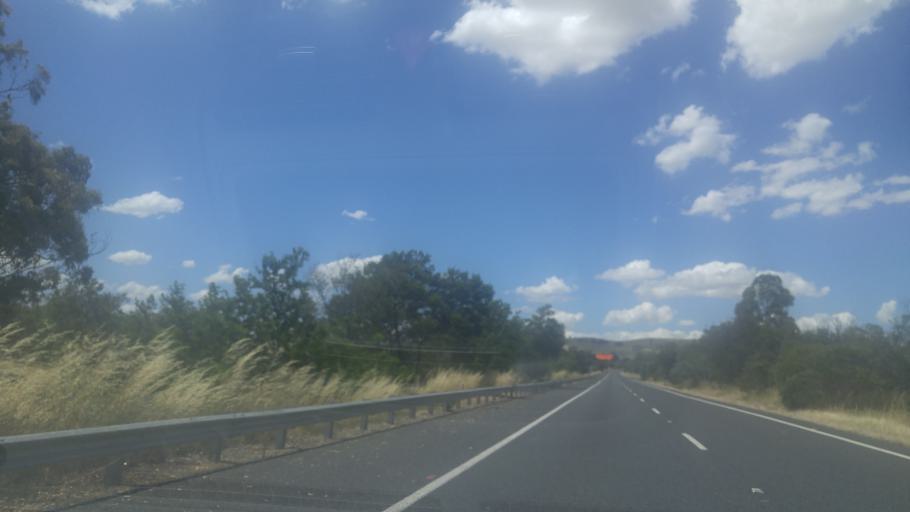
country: AU
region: New South Wales
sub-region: Yass Valley
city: Yass
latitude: -34.7860
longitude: 148.7035
